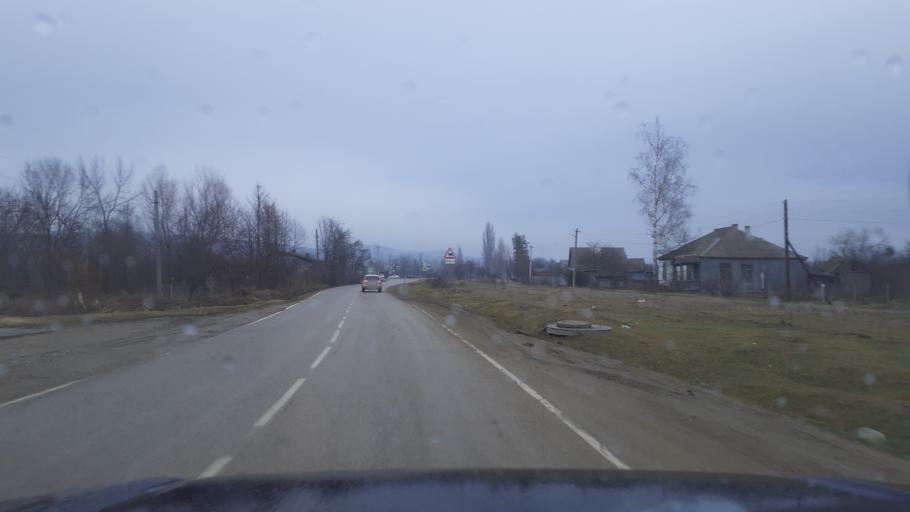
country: RU
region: Krasnodarskiy
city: Neftegorsk
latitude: 44.2483
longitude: 39.7660
